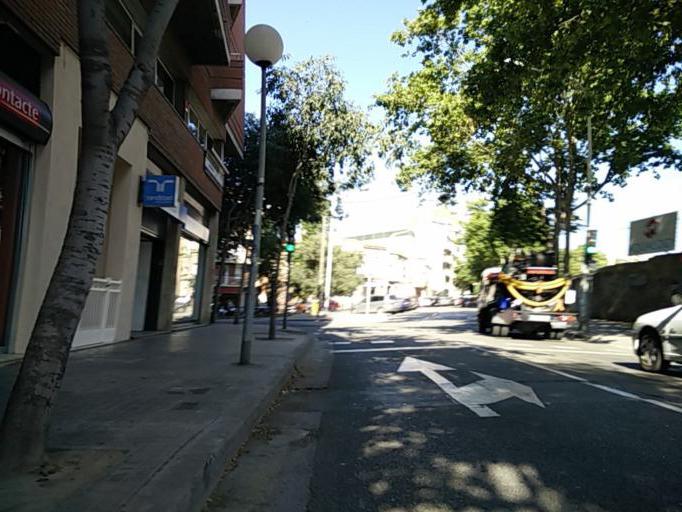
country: ES
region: Catalonia
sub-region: Provincia de Barcelona
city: Badalona
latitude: 41.4481
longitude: 2.2412
